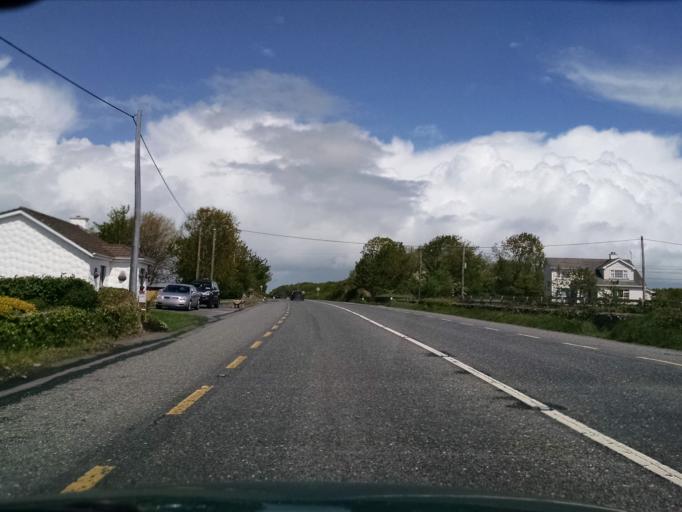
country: IE
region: Connaught
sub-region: County Galway
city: Oranmore
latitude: 53.2169
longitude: -8.8722
